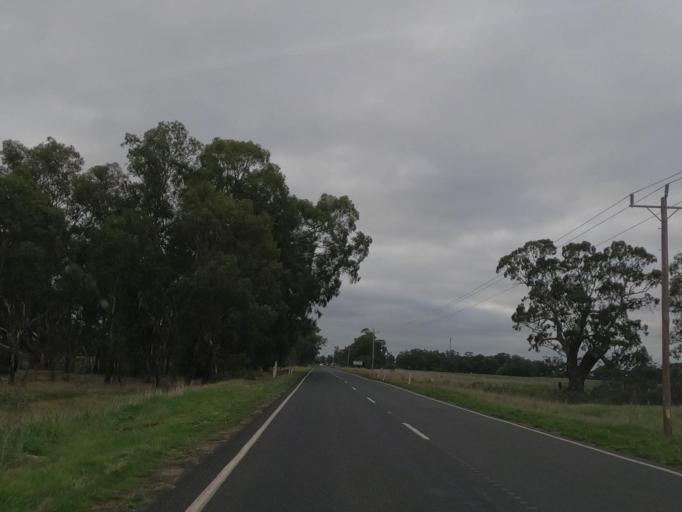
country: AU
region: Victoria
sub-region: Greater Bendigo
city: Long Gully
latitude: -36.4207
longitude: 143.9726
